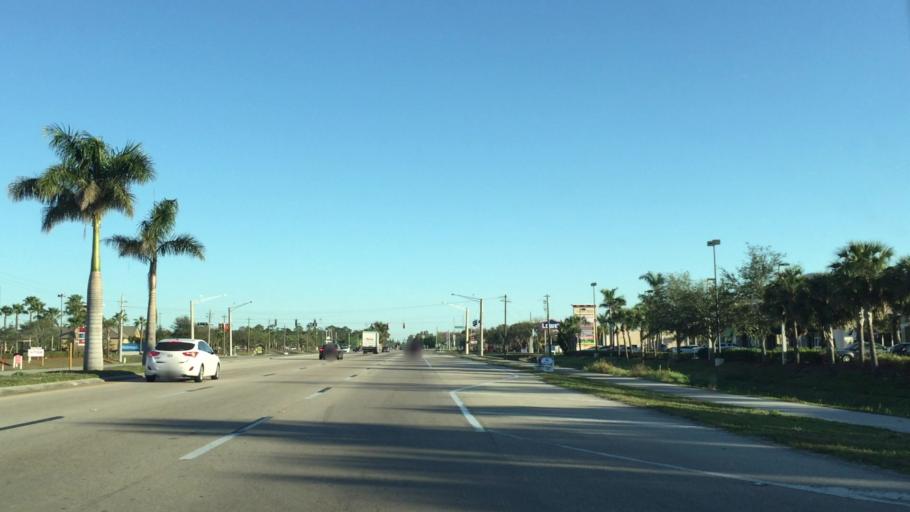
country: US
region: Florida
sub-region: Lee County
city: Fort Myers
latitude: 26.6074
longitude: -81.8111
